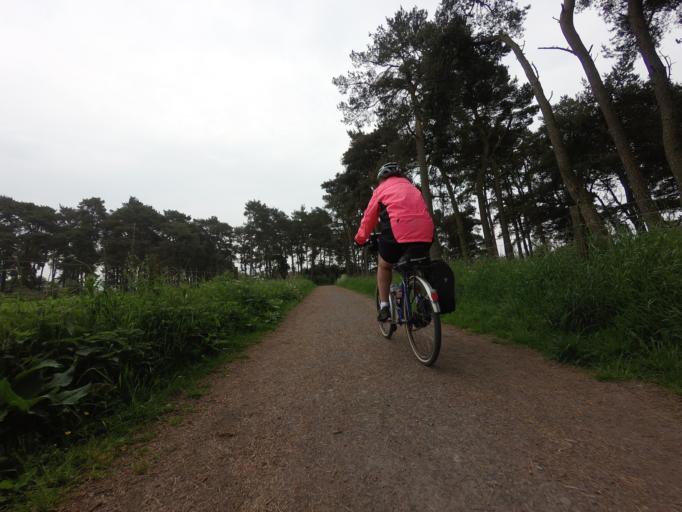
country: GB
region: Scotland
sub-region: Perth and Kinross
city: Milnathort
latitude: 56.2194
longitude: -3.3844
